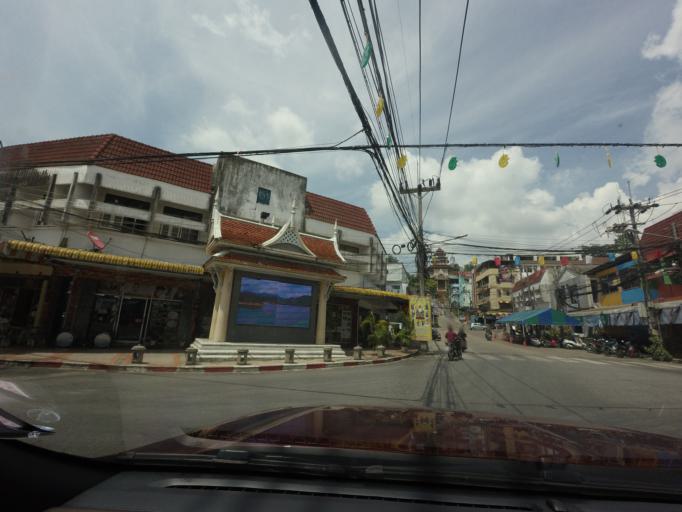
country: TH
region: Yala
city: Betong
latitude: 5.7718
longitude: 101.0716
